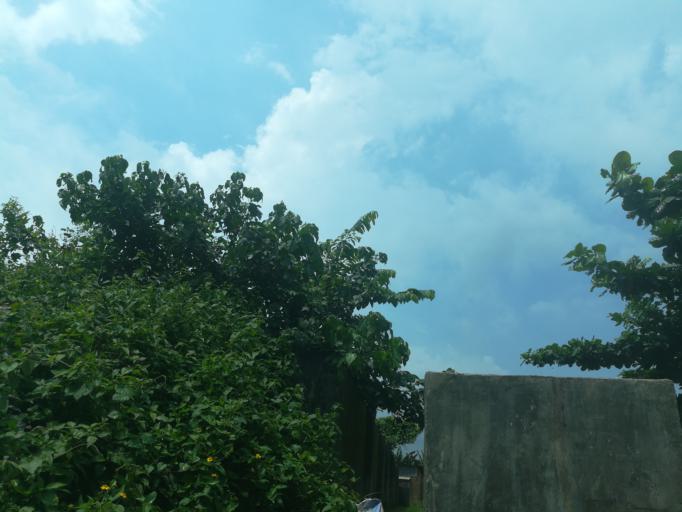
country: NG
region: Lagos
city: Ikorodu
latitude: 6.6717
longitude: 3.6673
